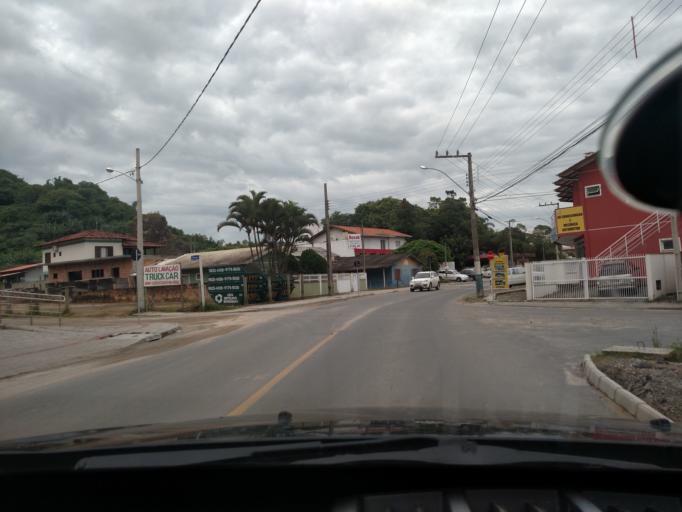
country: BR
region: Santa Catarina
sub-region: Porto Belo
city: Porto Belo
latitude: -27.1700
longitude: -48.5197
